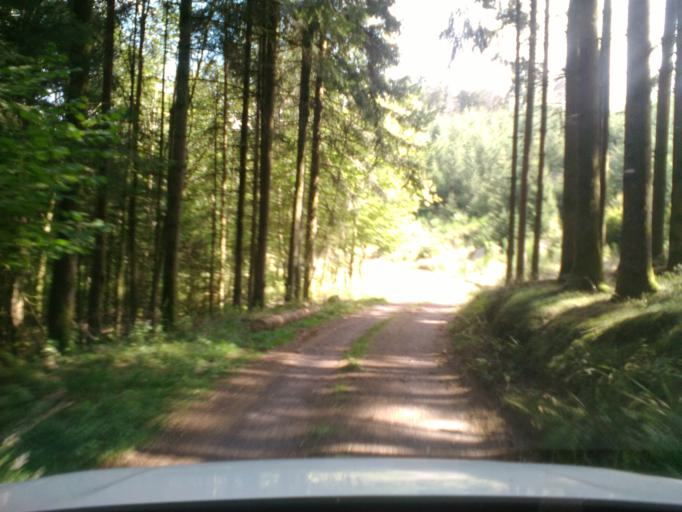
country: FR
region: Lorraine
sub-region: Departement des Vosges
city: Senones
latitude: 48.3512
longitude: 7.0438
